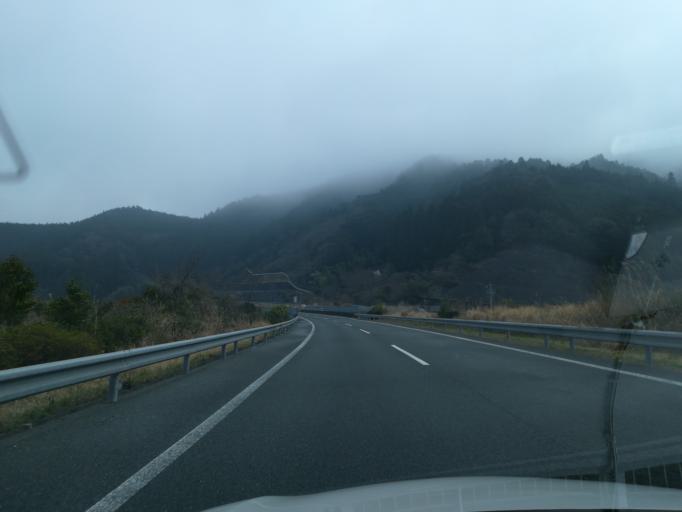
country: JP
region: Kochi
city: Kochi-shi
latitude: 33.7694
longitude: 133.6586
